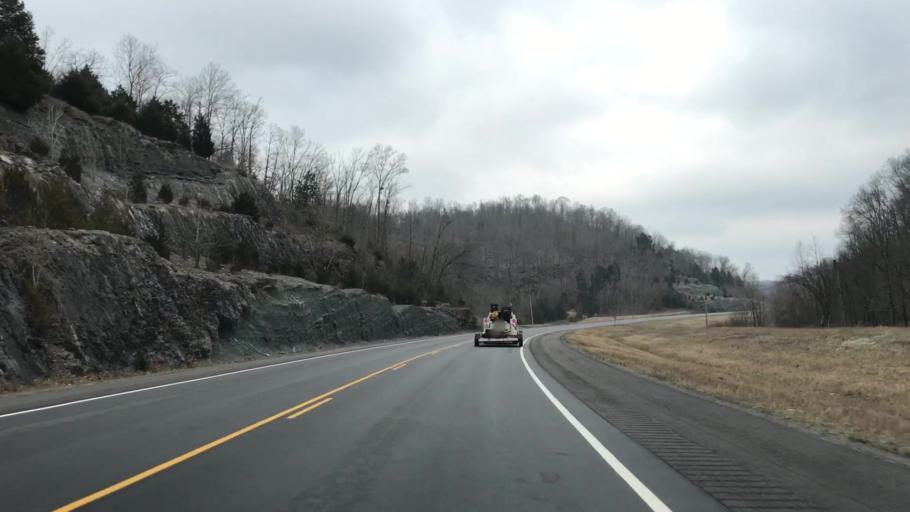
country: US
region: Kentucky
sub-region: Cumberland County
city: Burkesville
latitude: 36.9009
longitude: -85.4305
